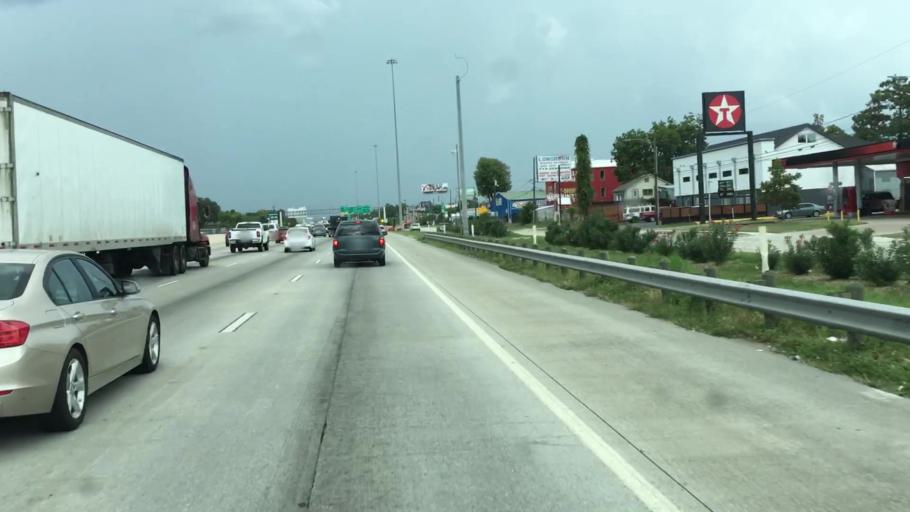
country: US
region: Texas
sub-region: Harris County
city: Houston
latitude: 29.8125
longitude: -95.4056
